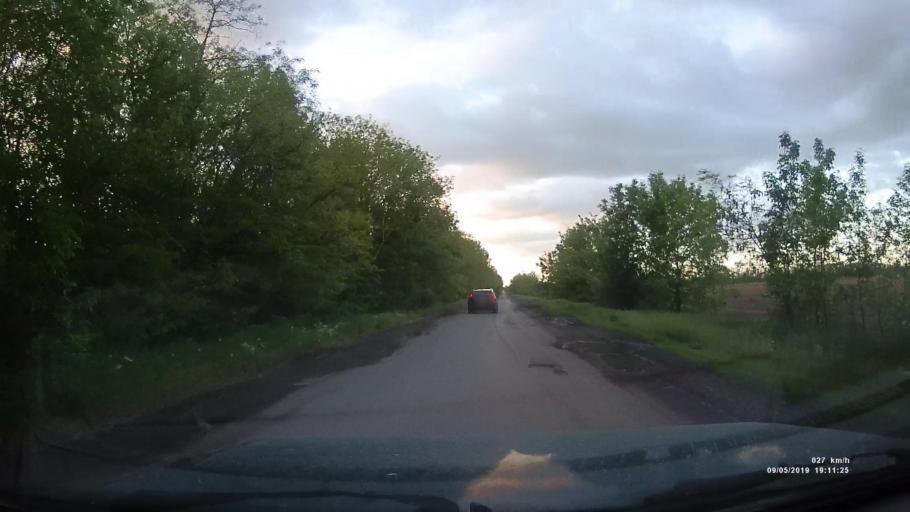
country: RU
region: Krasnodarskiy
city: Kanelovskaya
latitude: 46.7352
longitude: 39.2136
